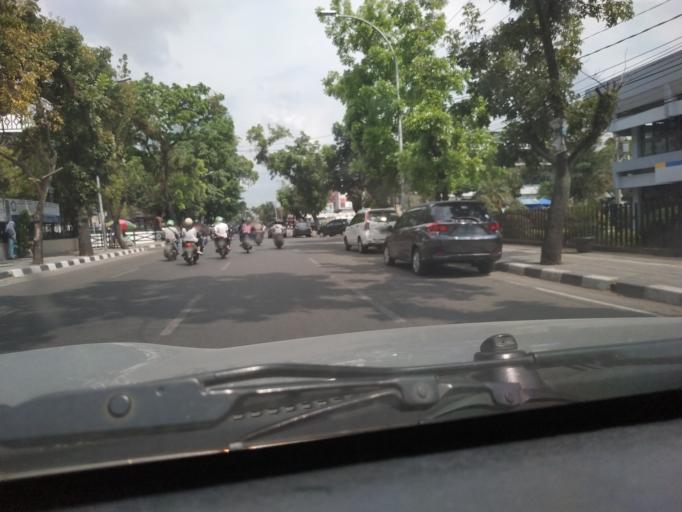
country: ID
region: North Sumatra
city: Medan
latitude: 3.5844
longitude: 98.6632
